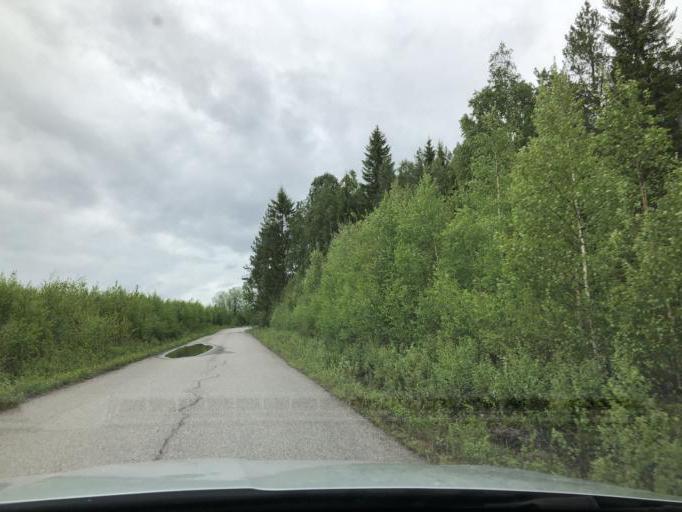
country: SE
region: Norrbotten
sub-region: Pitea Kommun
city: Roknas
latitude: 65.3875
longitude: 21.2703
